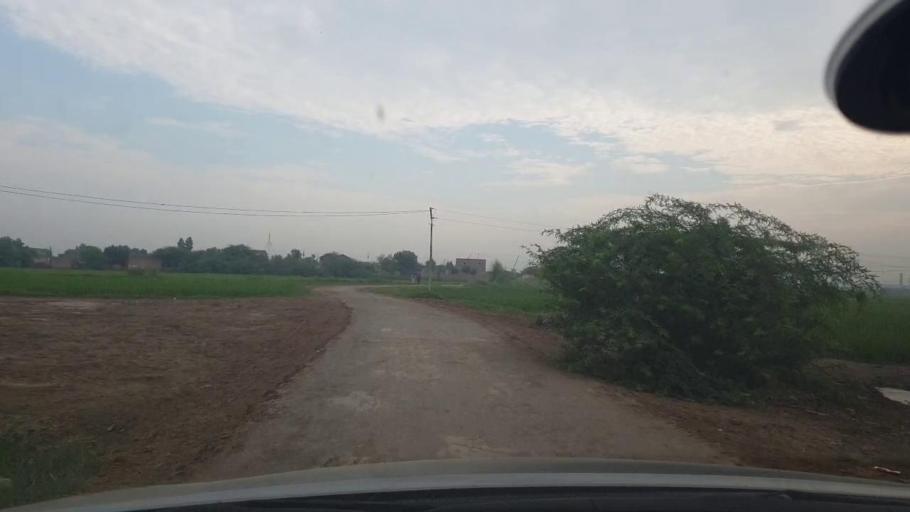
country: PK
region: Sindh
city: Jacobabad
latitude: 28.2919
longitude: 68.4192
